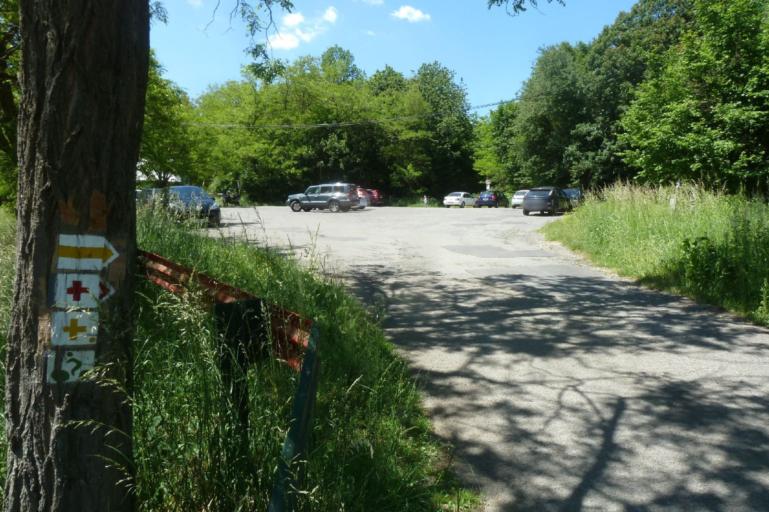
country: HU
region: Nograd
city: Somoskoujfalu
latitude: 48.1440
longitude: 19.8546
